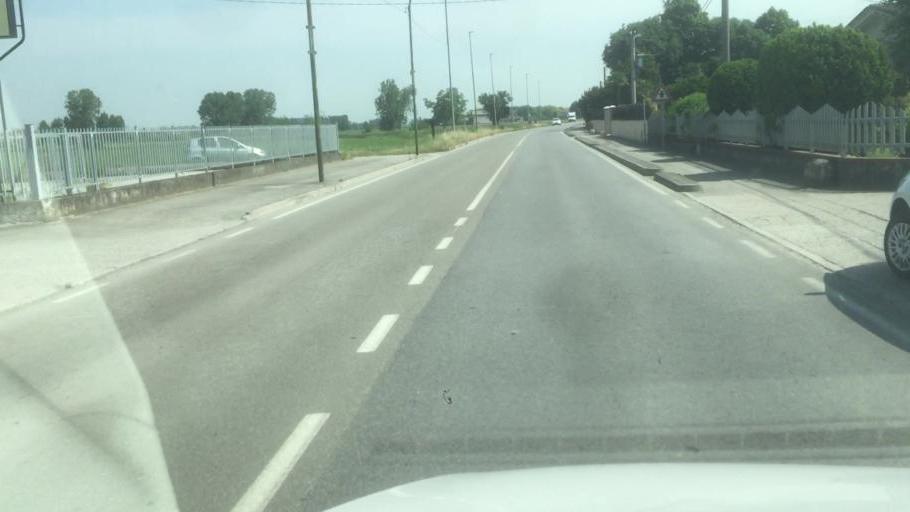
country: IT
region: Lombardy
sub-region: Provincia di Mantova
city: Casaloldo
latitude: 45.2488
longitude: 10.4592
